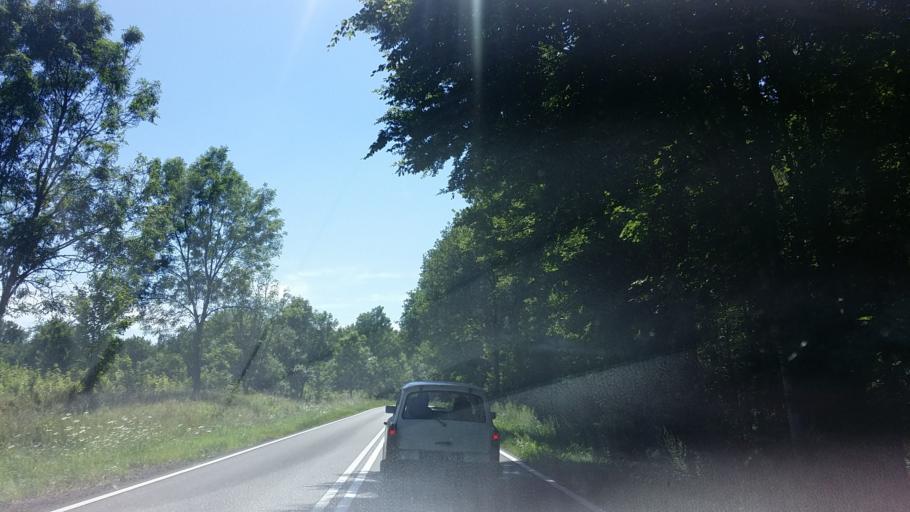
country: PL
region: West Pomeranian Voivodeship
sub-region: Powiat stargardzki
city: Insko
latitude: 53.4787
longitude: 15.5807
